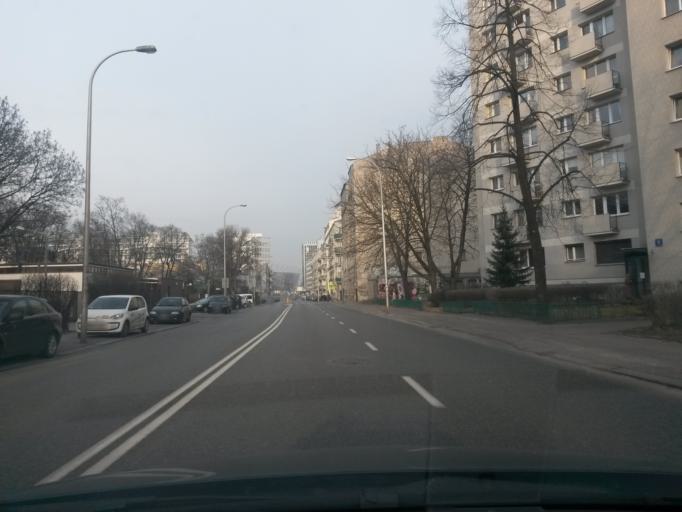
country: PL
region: Masovian Voivodeship
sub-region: Warszawa
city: Srodmiescie
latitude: 52.2307
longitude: 21.0346
